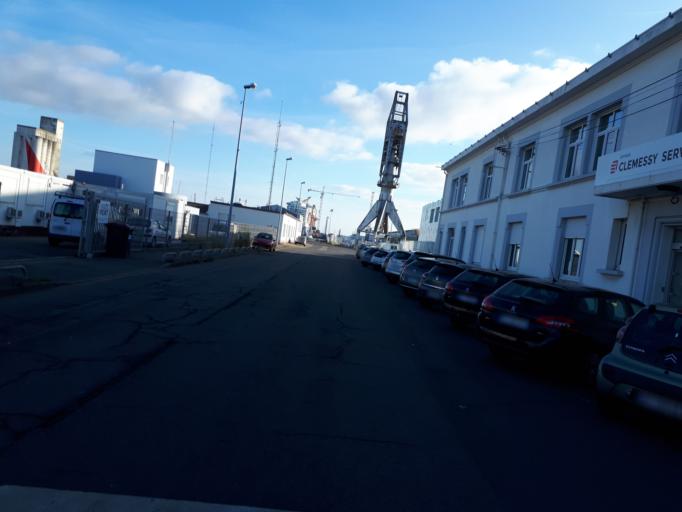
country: FR
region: Pays de la Loire
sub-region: Departement de la Loire-Atlantique
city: Saint-Nazaire
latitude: 47.2771
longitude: -2.1989
